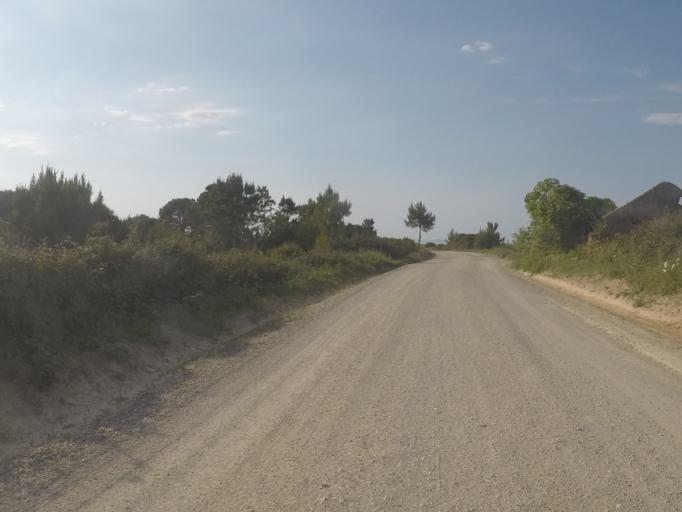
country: PT
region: Setubal
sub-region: Sesimbra
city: Sesimbra
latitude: 38.4449
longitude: -9.1972
